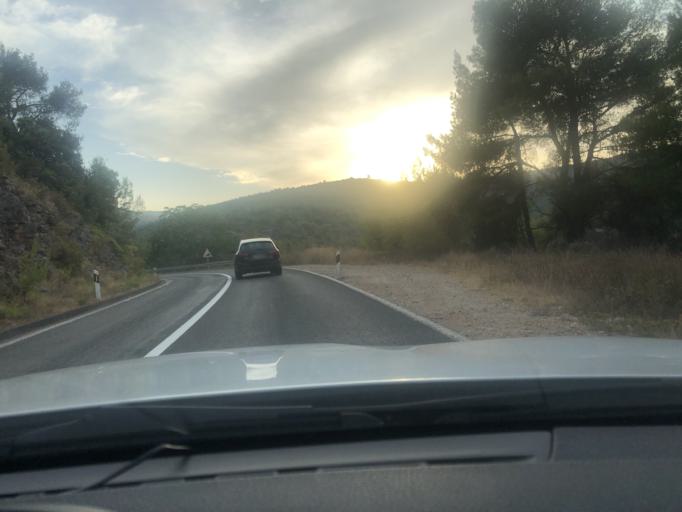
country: HR
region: Splitsko-Dalmatinska
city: Stari Grad
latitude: 43.1714
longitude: 16.5656
